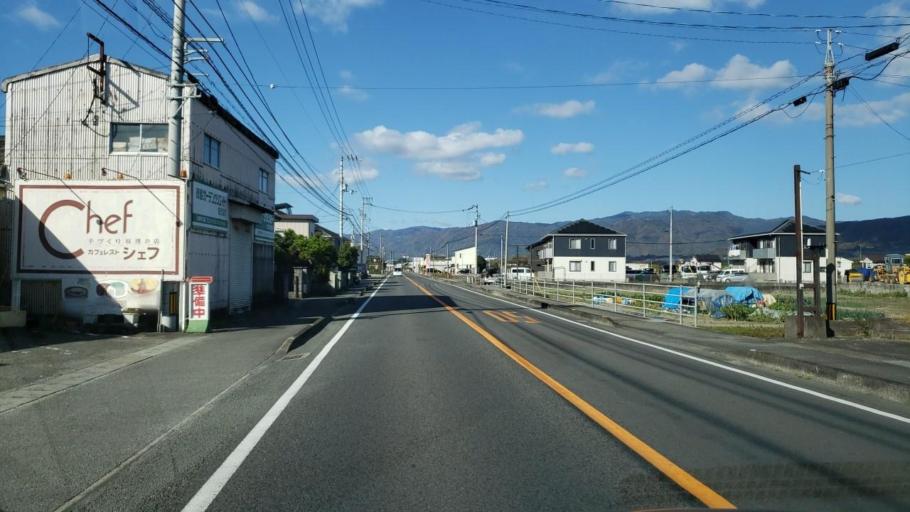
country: JP
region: Tokushima
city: Wakimachi
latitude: 34.0586
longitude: 134.2203
